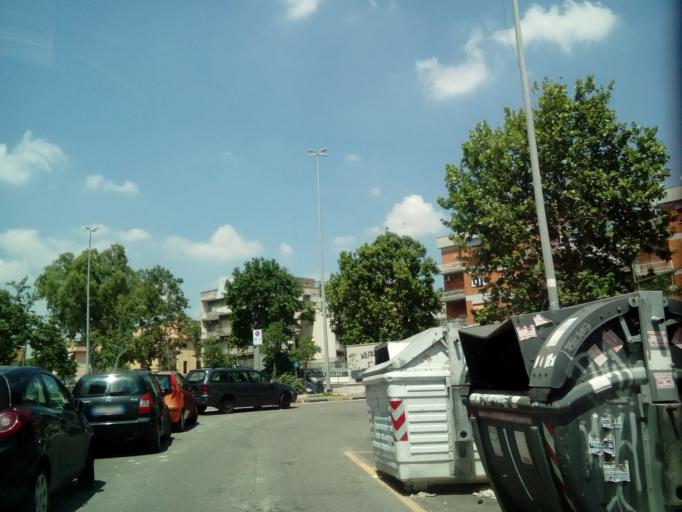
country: IT
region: Latium
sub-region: Citta metropolitana di Roma Capitale
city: Rome
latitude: 41.8768
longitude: 12.5670
